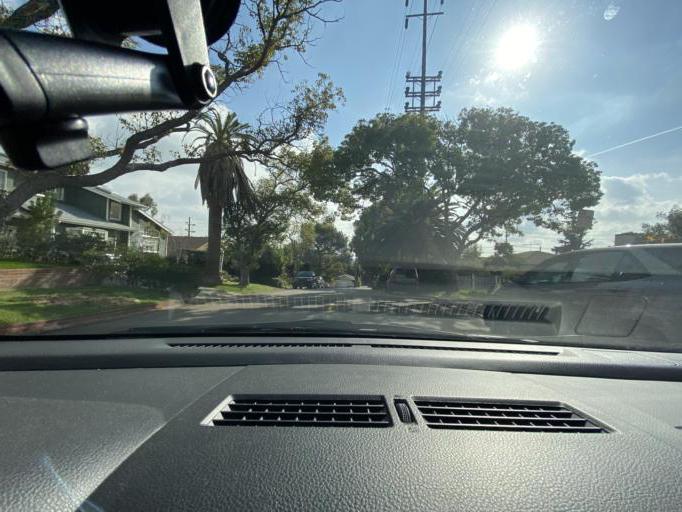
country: US
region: California
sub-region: Los Angeles County
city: Culver City
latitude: 34.0191
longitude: -118.4179
